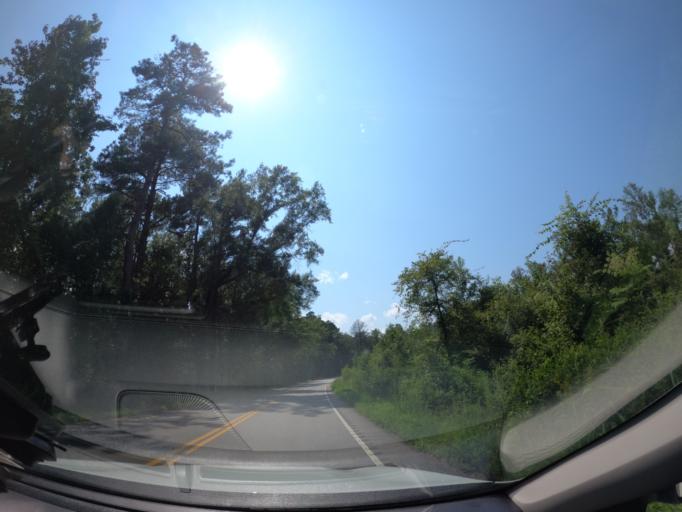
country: US
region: South Carolina
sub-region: Richland County
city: Hopkins
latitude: 33.8408
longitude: -80.8574
